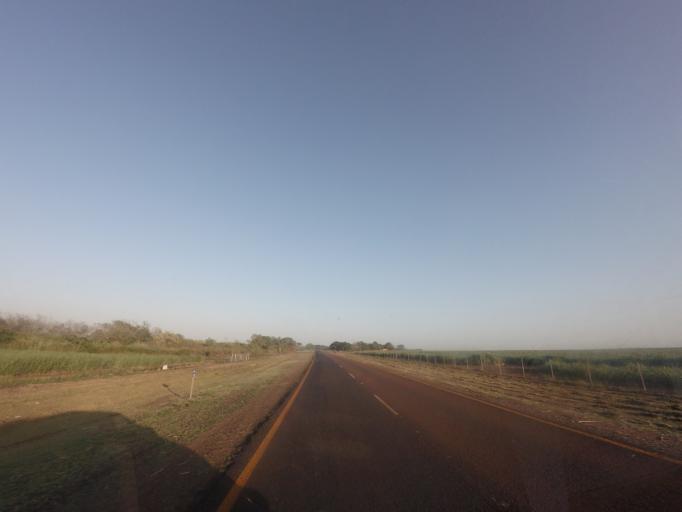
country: ZA
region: Mpumalanga
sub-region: Ehlanzeni District
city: Komatipoort
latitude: -25.4176
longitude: 31.9394
